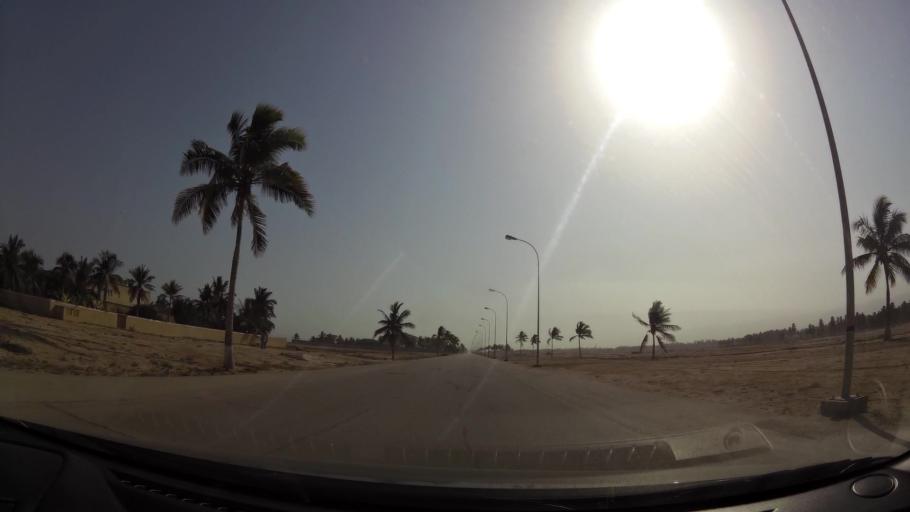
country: OM
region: Zufar
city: Salalah
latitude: 16.9953
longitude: 54.0598
